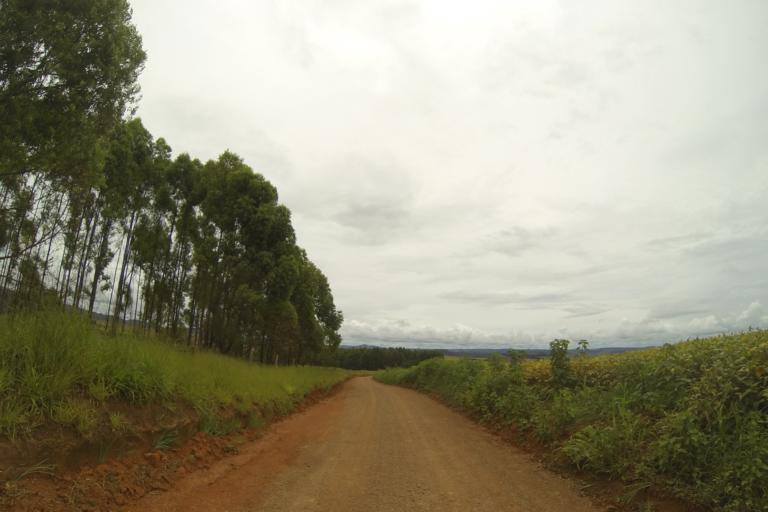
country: BR
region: Minas Gerais
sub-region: Ibia
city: Ibia
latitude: -19.7420
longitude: -46.6348
